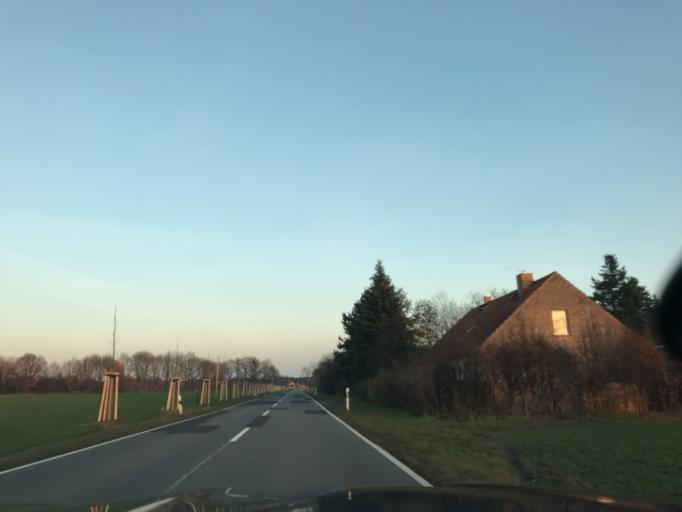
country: DE
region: Brandenburg
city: Nennhausen
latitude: 52.5073
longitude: 12.4811
